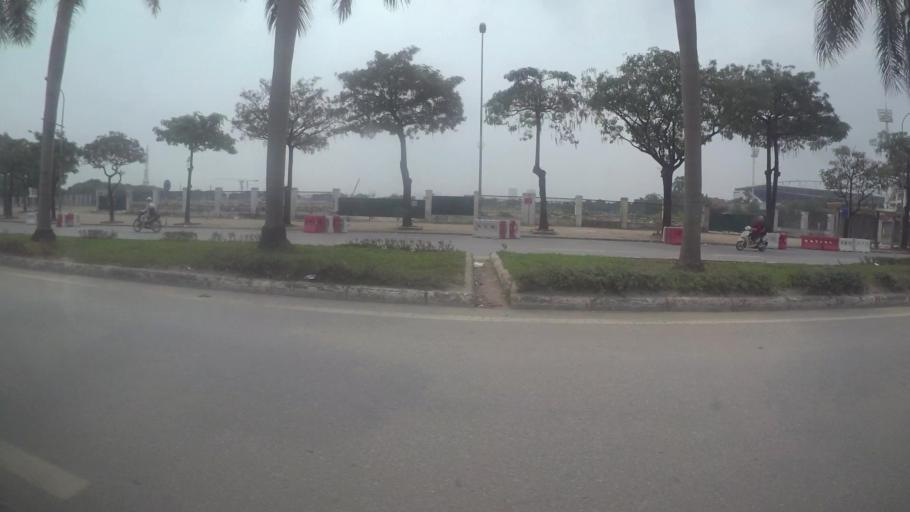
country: VN
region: Ha Noi
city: Cau Dien
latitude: 21.0182
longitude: 105.7665
